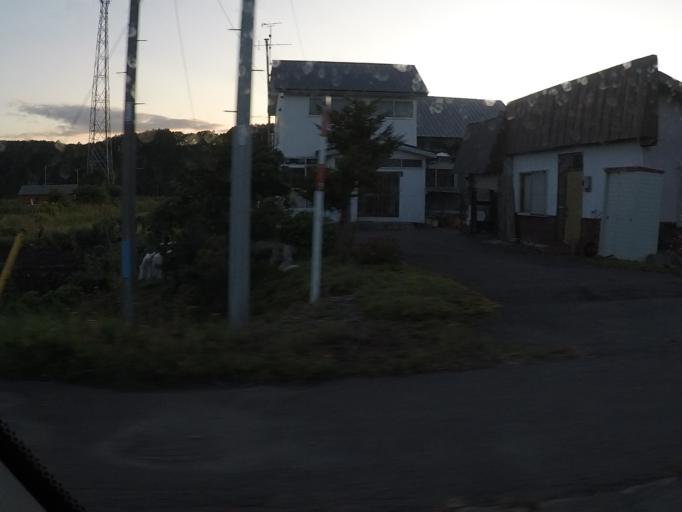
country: JP
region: Hokkaido
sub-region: Asahikawa-shi
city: Asahikawa
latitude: 43.6455
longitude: 142.4491
